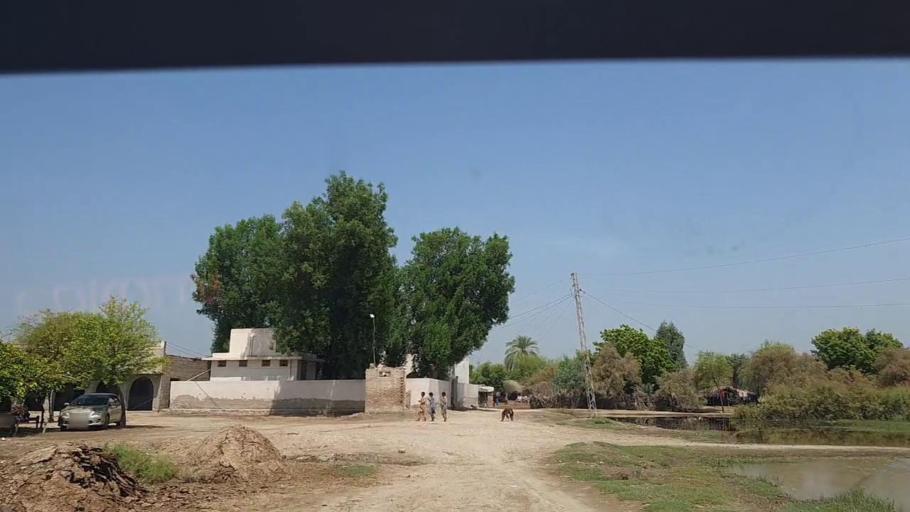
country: PK
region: Sindh
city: Ghauspur
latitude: 28.1882
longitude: 69.0883
